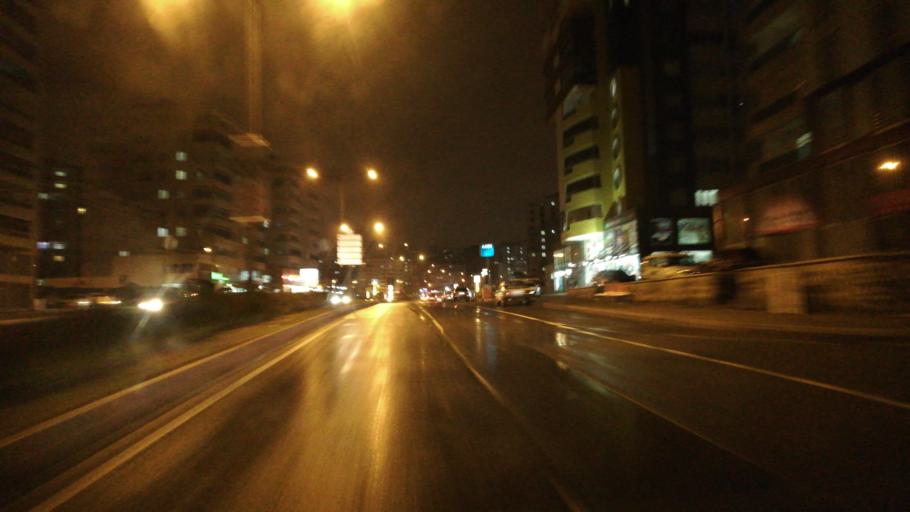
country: TR
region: Kahramanmaras
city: Kahramanmaras
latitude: 37.5806
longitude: 36.8637
